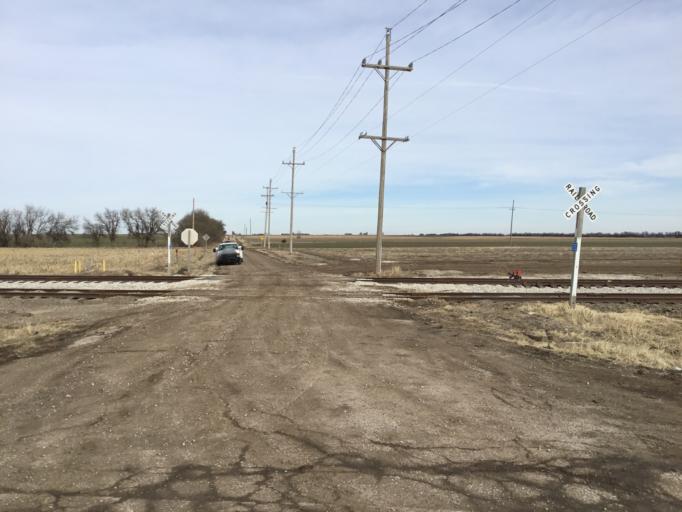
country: US
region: Kansas
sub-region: McPherson County
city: Inman
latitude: 38.3760
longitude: -97.8141
